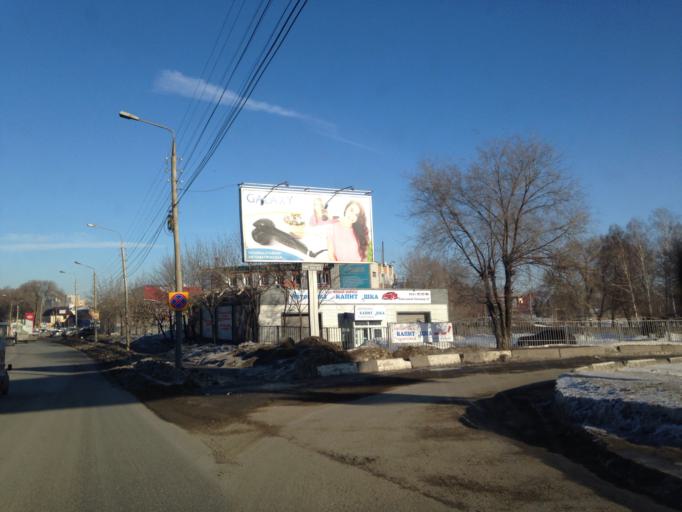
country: RU
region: Ulyanovsk
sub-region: Ulyanovskiy Rayon
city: Ulyanovsk
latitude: 54.2946
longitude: 48.3180
